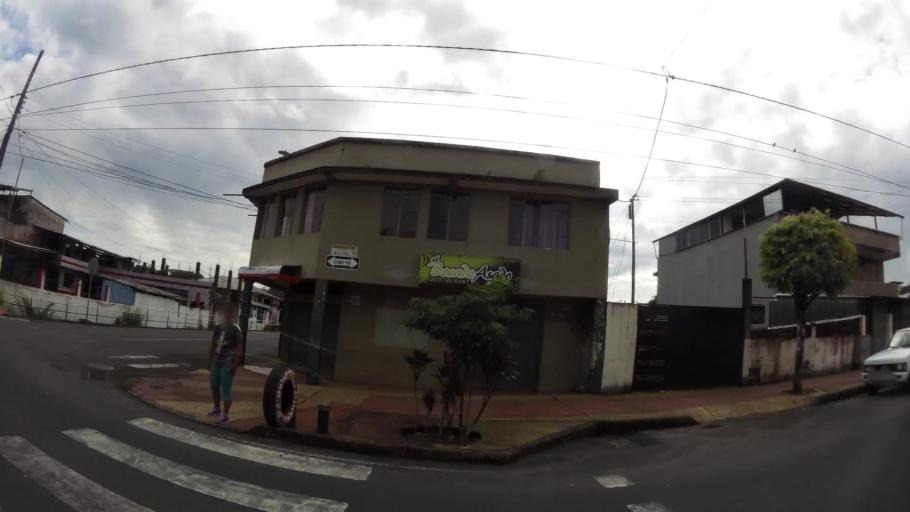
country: EC
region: Pastaza
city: Puyo
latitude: -1.4808
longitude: -78.0001
